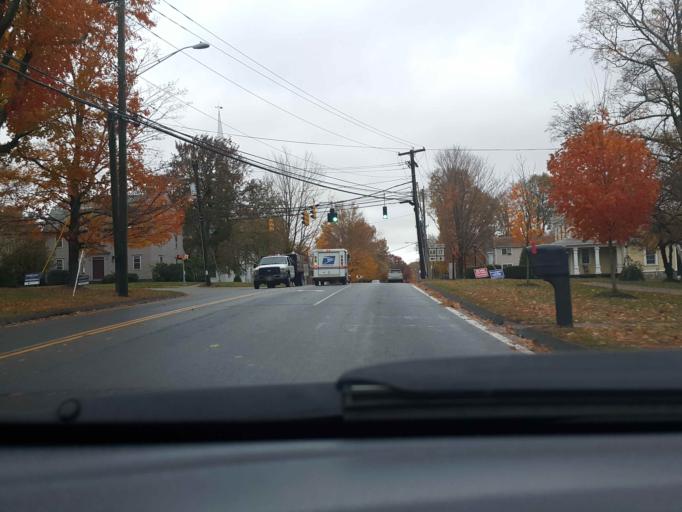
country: US
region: Connecticut
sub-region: Middlesex County
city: Durham
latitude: 41.4774
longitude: -72.6810
